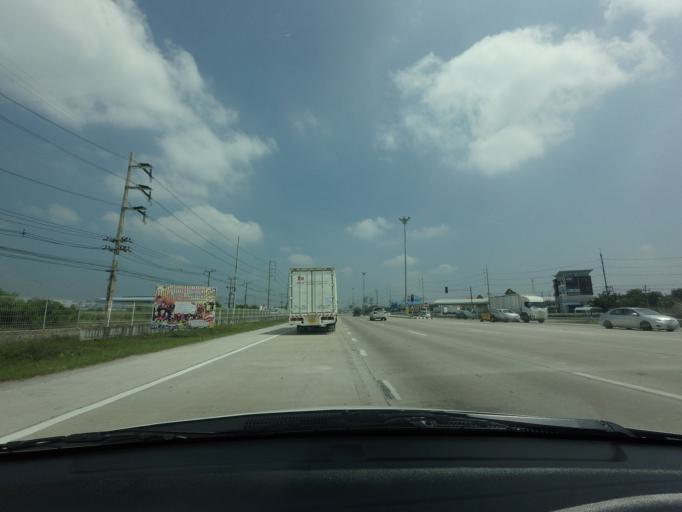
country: TH
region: Chachoengsao
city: Bang Pakong
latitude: 13.5601
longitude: 100.9948
